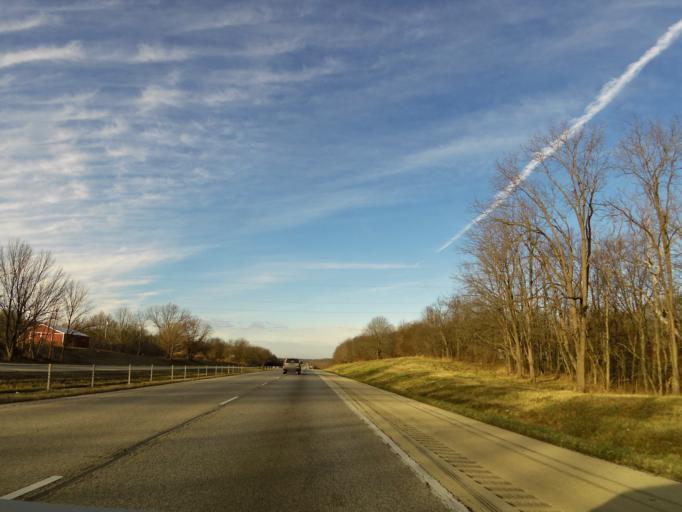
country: US
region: Illinois
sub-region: Vermilion County
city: Danville
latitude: 40.1152
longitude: -87.5723
